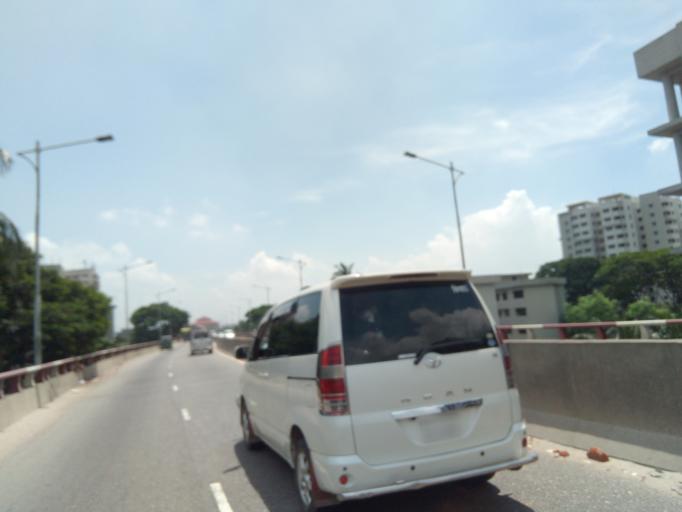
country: BD
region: Dhaka
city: Tungi
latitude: 23.8165
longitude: 90.4008
